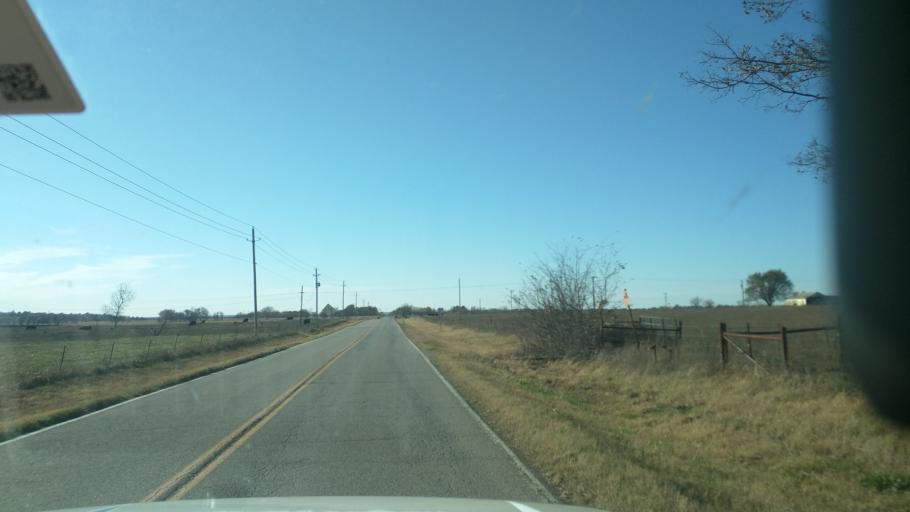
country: US
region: Oklahoma
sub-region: Nowata County
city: Nowata
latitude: 36.7716
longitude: -95.5415
